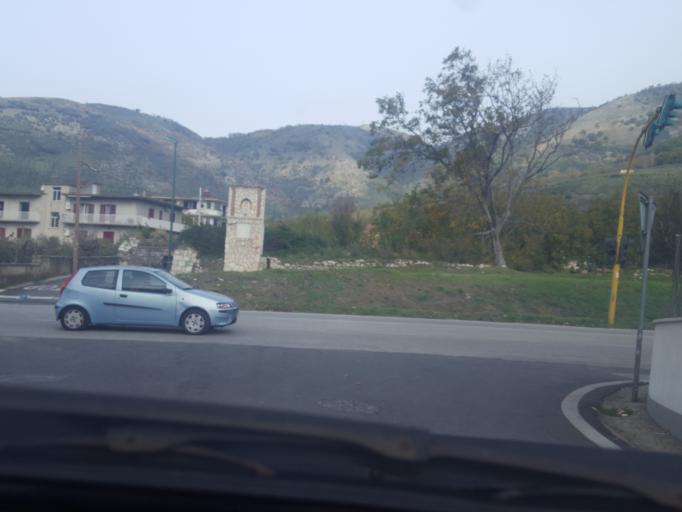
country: IT
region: Campania
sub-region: Provincia di Caserta
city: Arienzo
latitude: 41.0306
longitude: 14.4934
